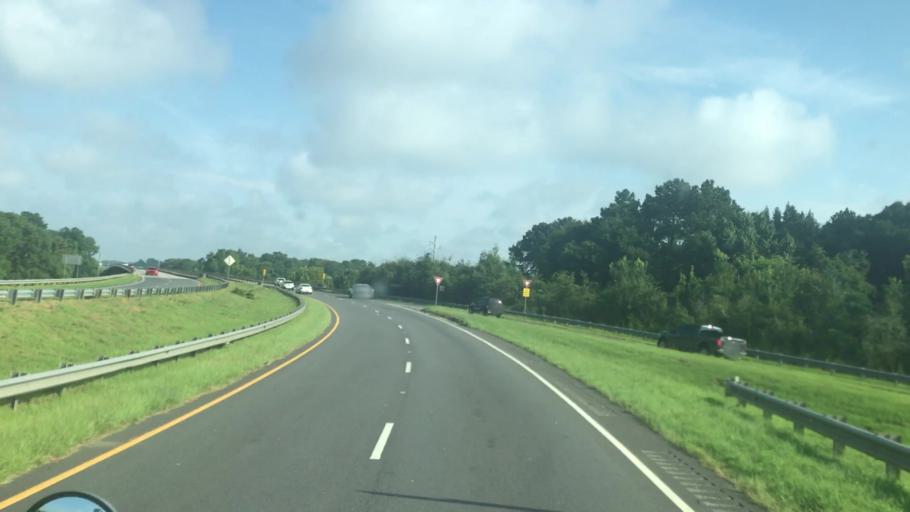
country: US
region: Georgia
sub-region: Decatur County
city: Bainbridge
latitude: 30.9043
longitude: -84.5869
